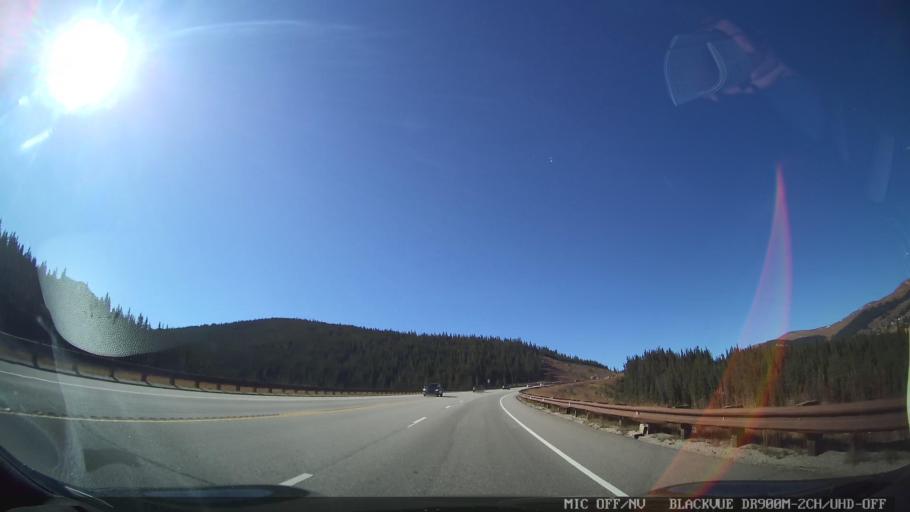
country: US
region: Colorado
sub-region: Summit County
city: Breckenridge
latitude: 39.4336
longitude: -106.1633
